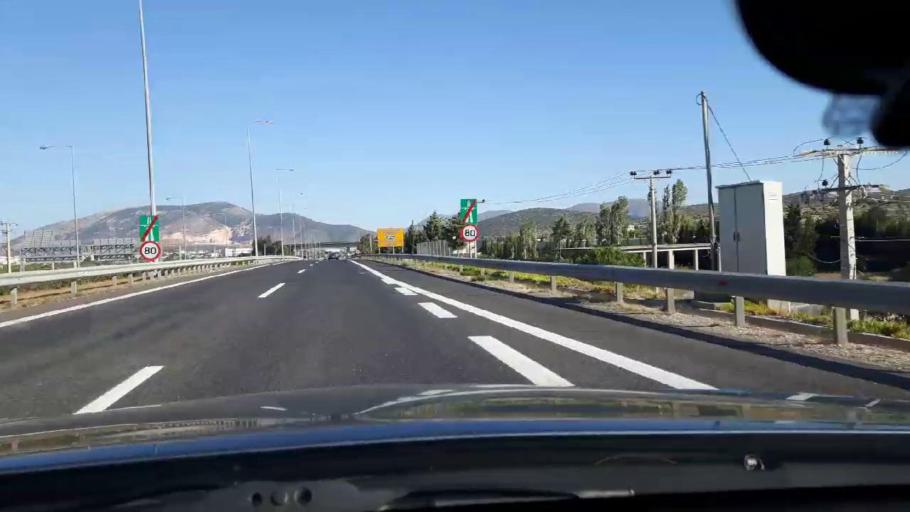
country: GR
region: Attica
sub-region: Nomarchia Anatolikis Attikis
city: Markopoulo
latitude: 37.8959
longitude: 23.9115
